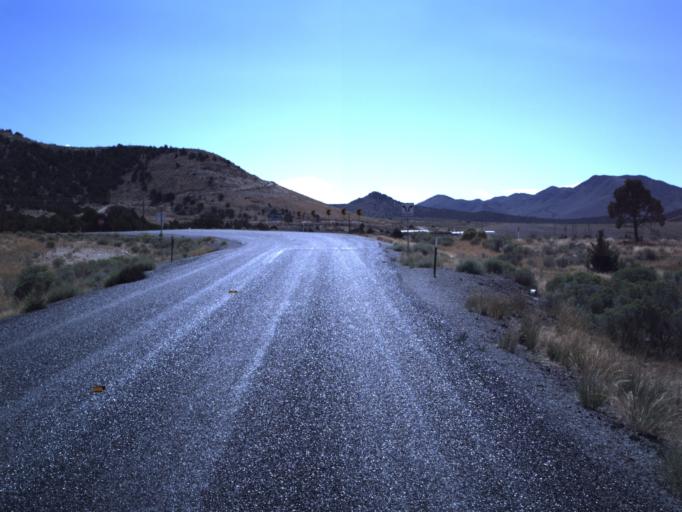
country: US
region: Utah
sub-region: Juab County
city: Mona
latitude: 39.9201
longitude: -112.1468
